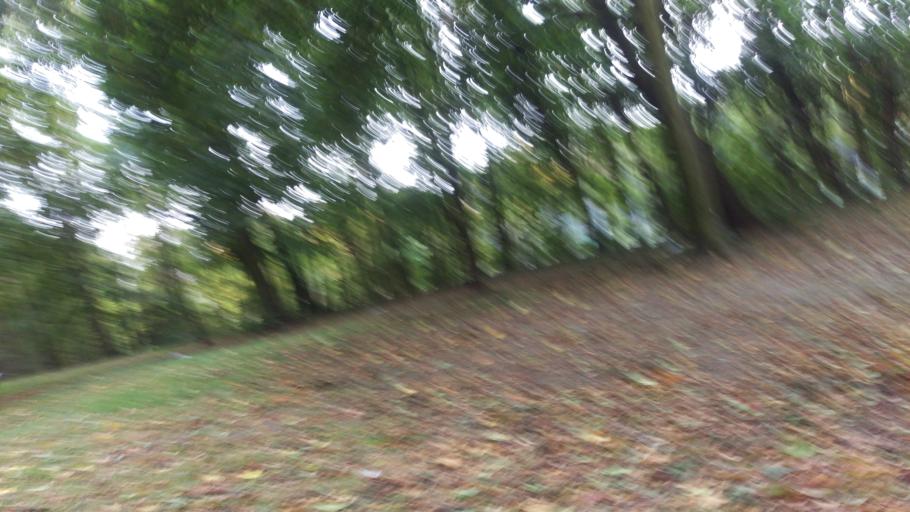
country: PL
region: West Pomeranian Voivodeship
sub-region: Szczecin
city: Szczecin
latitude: 53.3948
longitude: 14.6746
